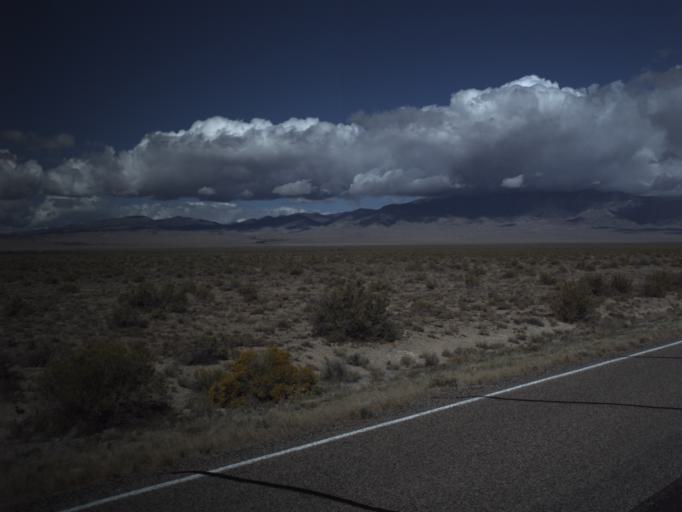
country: US
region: Nevada
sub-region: White Pine County
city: McGill
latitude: 38.9980
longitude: -114.0347
